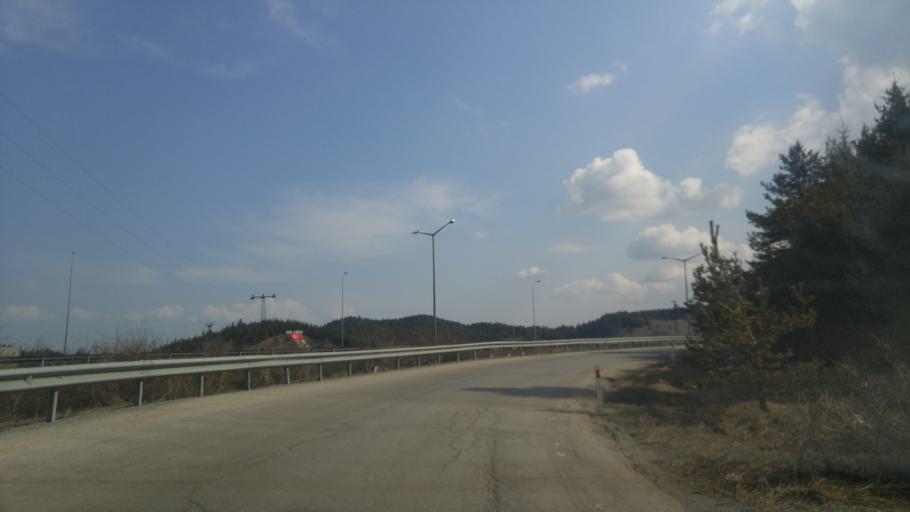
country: TR
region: Bolu
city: Gerede
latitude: 40.6113
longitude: 32.2553
